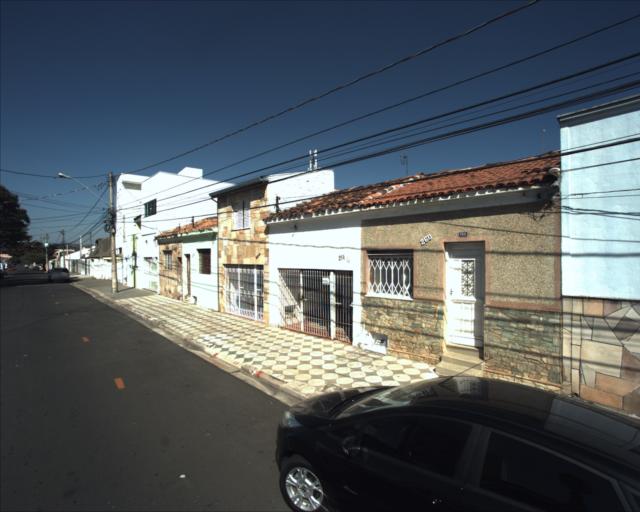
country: BR
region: Sao Paulo
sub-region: Sorocaba
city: Sorocaba
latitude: -23.5059
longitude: -47.4426
